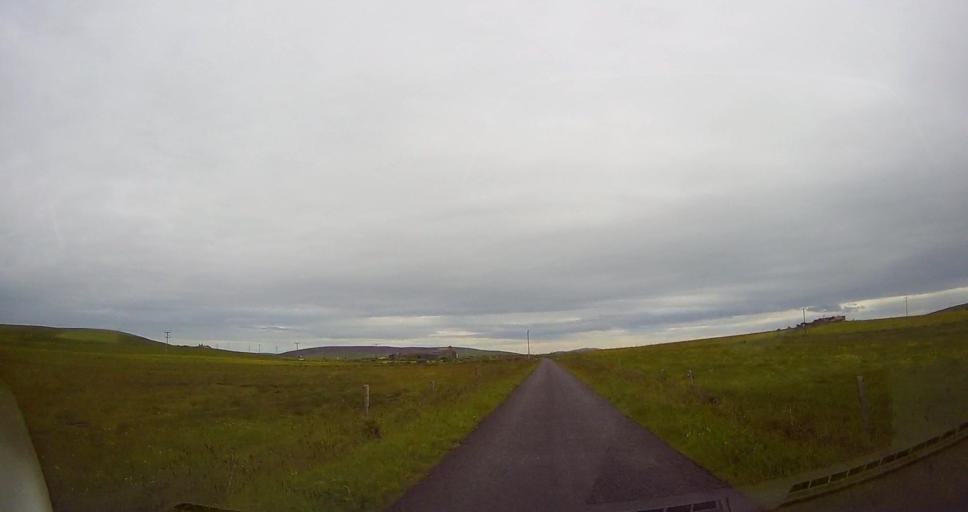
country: GB
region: Scotland
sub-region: Orkney Islands
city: Stromness
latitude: 59.1237
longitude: -3.2785
